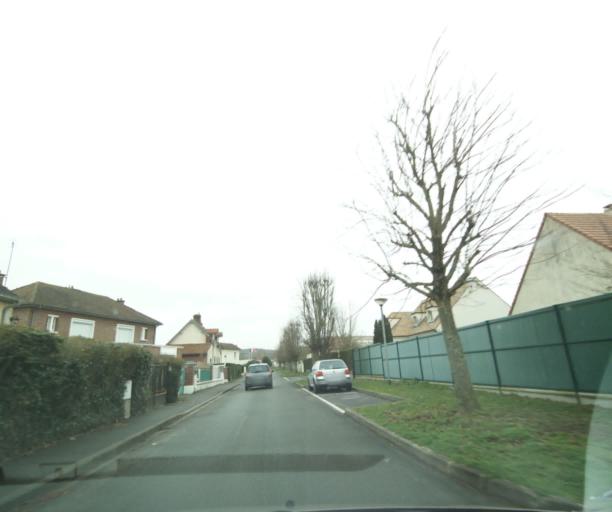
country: FR
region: Picardie
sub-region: Departement de l'Oise
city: Noyon
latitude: 49.5743
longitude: 2.9916
